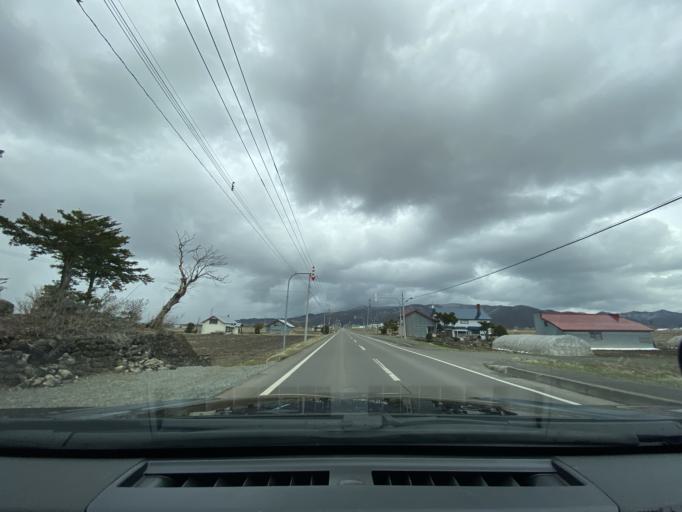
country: JP
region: Hokkaido
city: Nayoro
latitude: 44.1161
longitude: 142.4806
